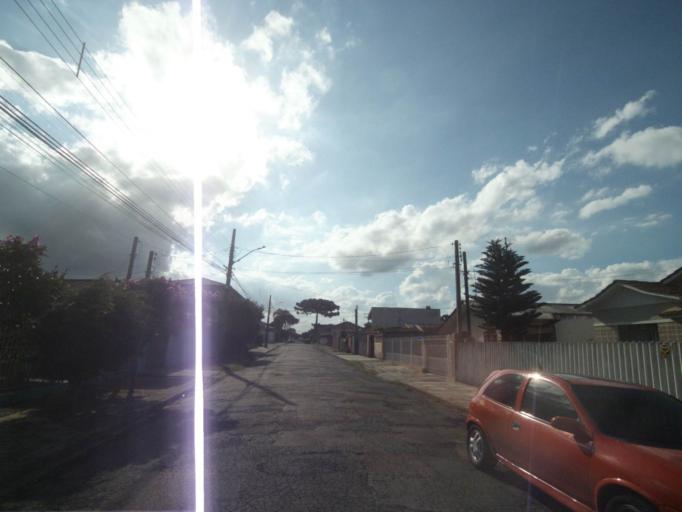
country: BR
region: Parana
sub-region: Pinhais
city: Pinhais
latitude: -25.4389
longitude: -49.2170
